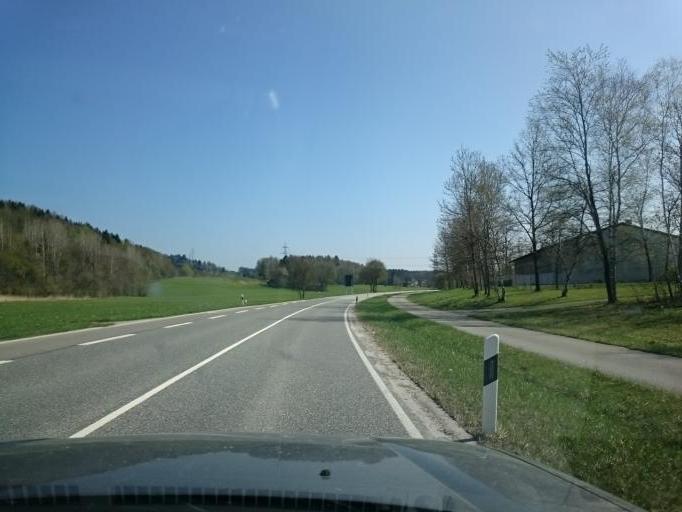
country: DE
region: Bavaria
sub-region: Upper Bavaria
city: Grossweil
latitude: 47.6731
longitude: 11.2850
